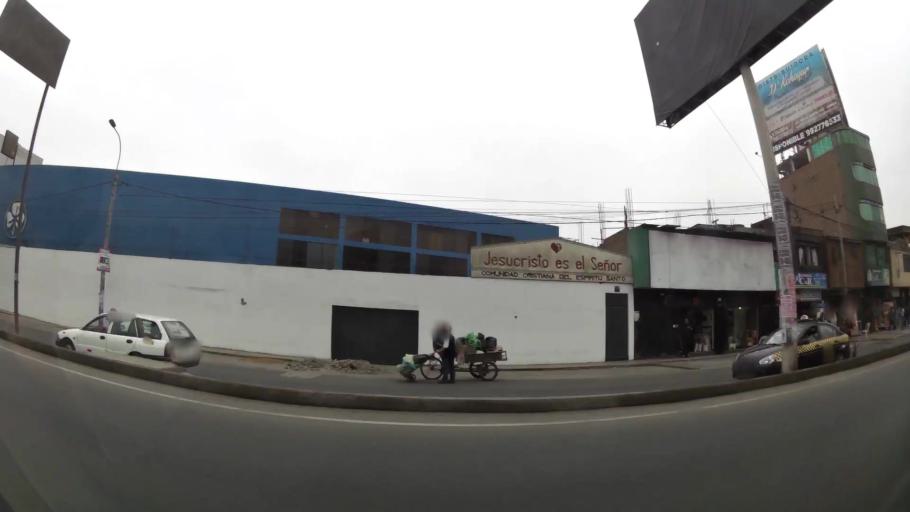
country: PE
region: Lima
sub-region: Lima
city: Independencia
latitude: -11.9390
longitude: -77.0501
